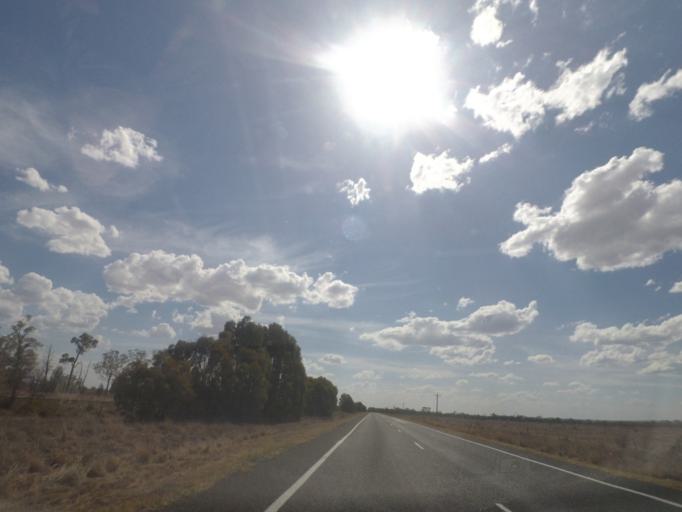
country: AU
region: New South Wales
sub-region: Moree Plains
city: Boggabilla
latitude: -28.4150
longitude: 151.1316
